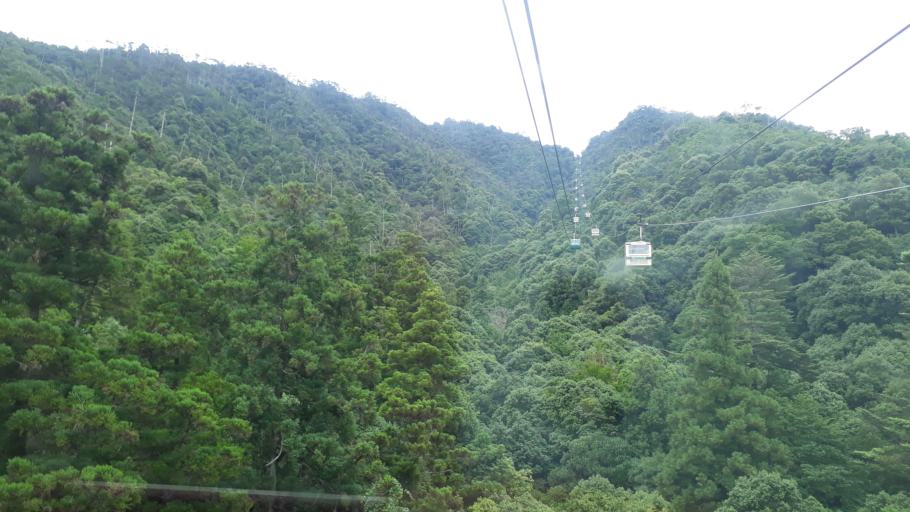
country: JP
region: Hiroshima
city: Miyajima
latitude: 34.2922
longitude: 132.3269
